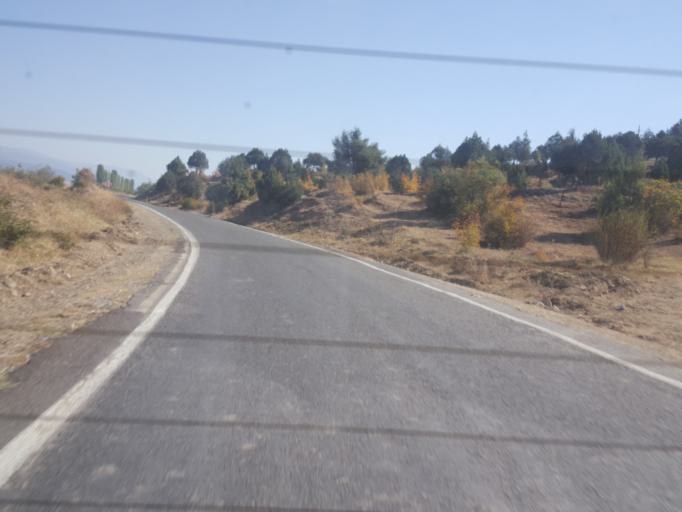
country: TR
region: Kastamonu
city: Tosya
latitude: 40.9950
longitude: 34.1346
